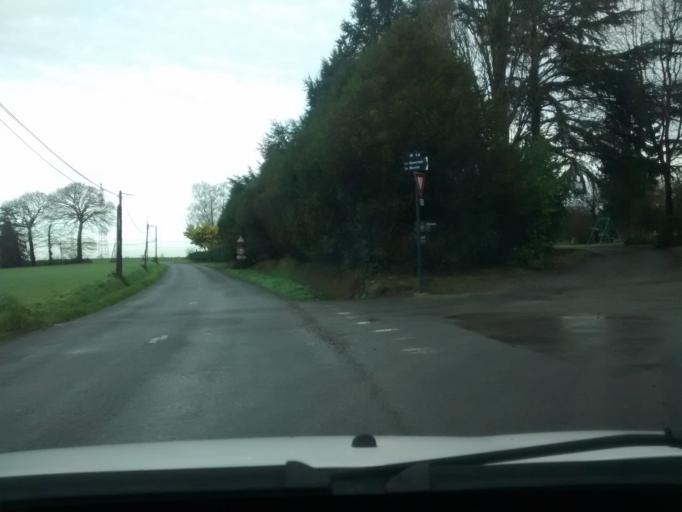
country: FR
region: Brittany
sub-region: Departement d'Ille-et-Vilaine
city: Montgermont
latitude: 48.1373
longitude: -1.7146
